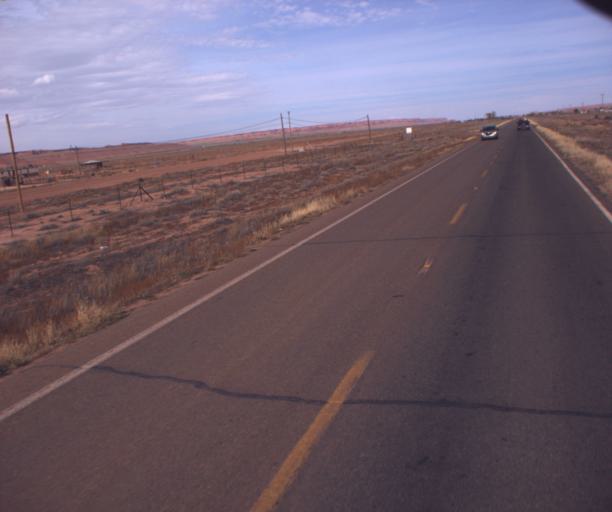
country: US
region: Arizona
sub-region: Apache County
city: Many Farms
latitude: 36.3901
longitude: -109.6104
